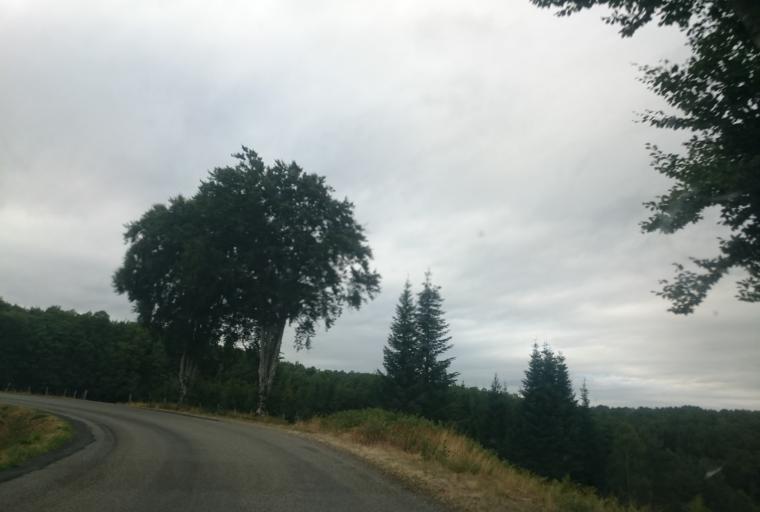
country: FR
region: Auvergne
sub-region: Departement du Cantal
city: Saint-Mamet-la-Salvetat
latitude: 44.8428
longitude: 2.3305
